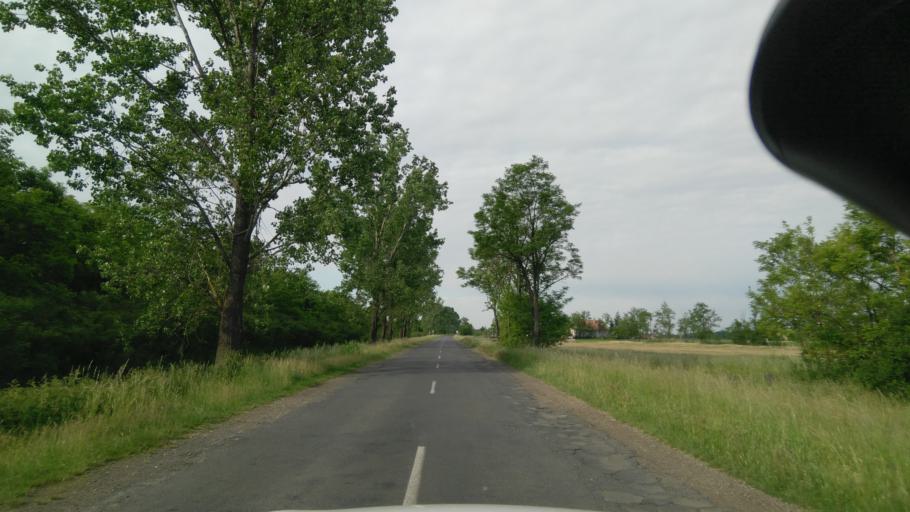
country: HU
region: Bekes
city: Gyula
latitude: 46.6059
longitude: 21.2425
